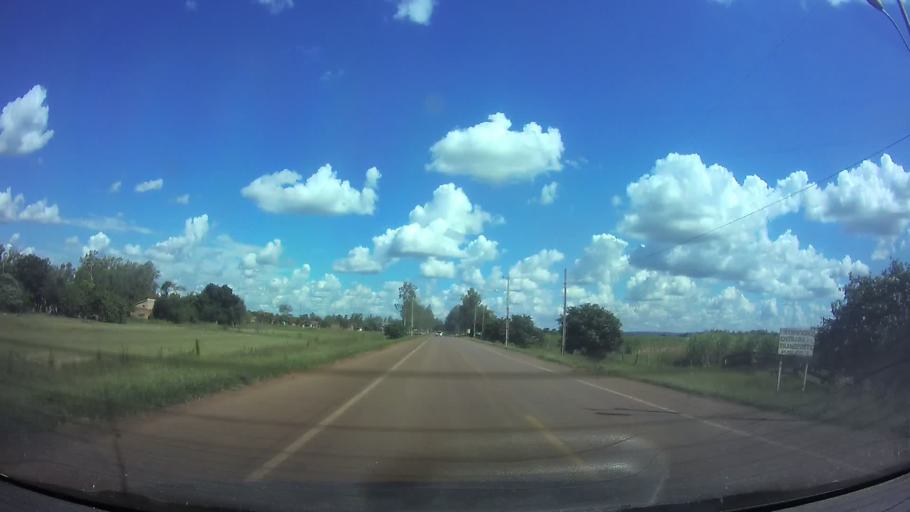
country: PY
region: Guaira
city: Coronel Martinez
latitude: -25.7810
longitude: -56.6499
